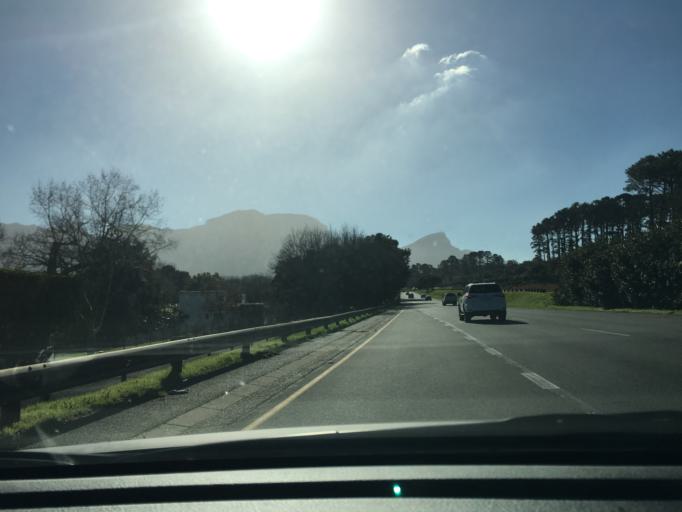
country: ZA
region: Western Cape
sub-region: City of Cape Town
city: Claremont
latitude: -34.0128
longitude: 18.4534
